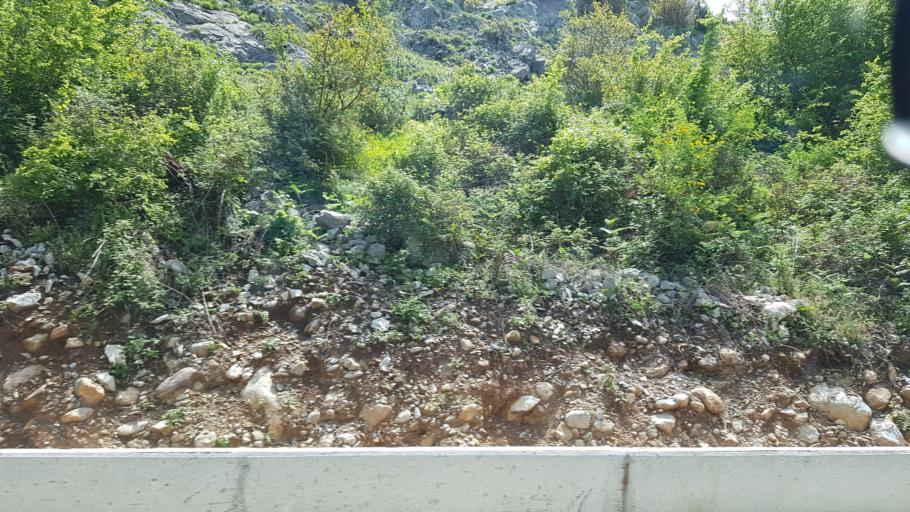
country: AL
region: Shkoder
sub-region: Rrethi i Shkodres
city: Guri i Zi
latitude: 42.1276
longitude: 19.6070
